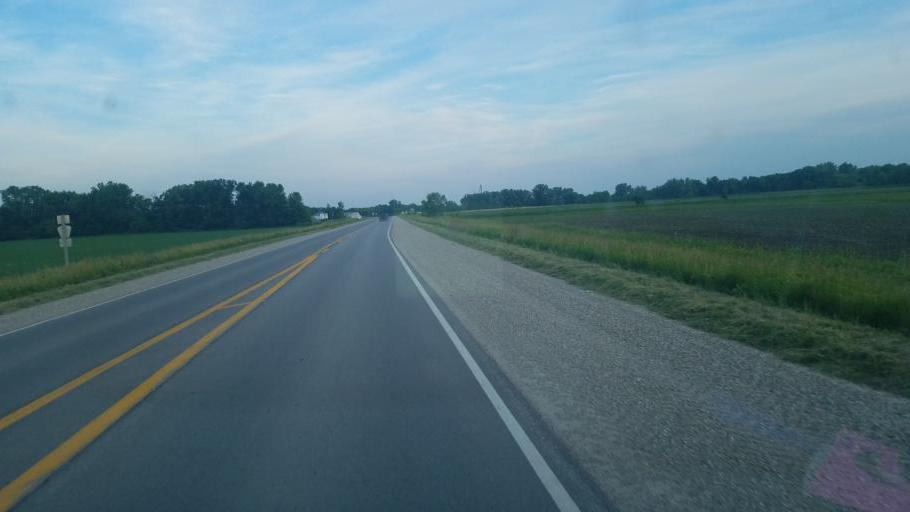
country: US
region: Iowa
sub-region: Benton County
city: Belle Plaine
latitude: 41.9050
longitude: -92.2954
